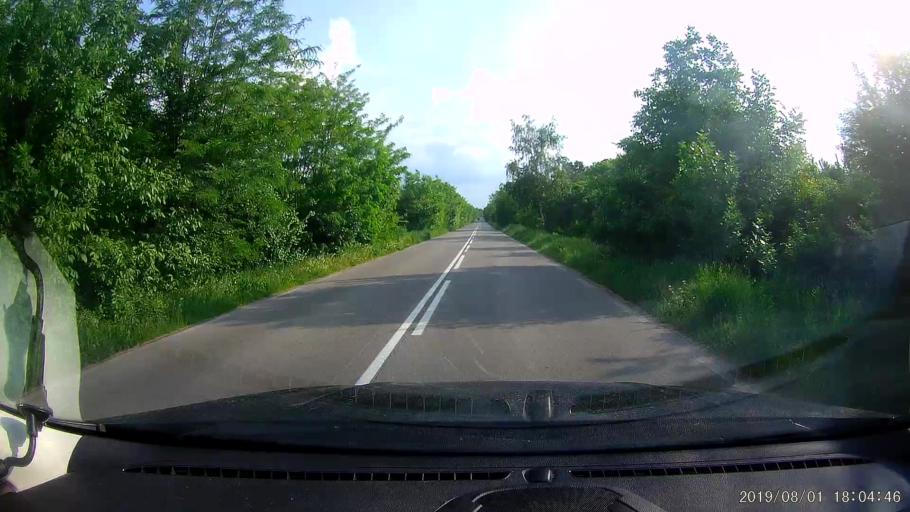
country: BG
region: Silistra
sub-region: Obshtina Alfatar
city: Alfatar
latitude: 43.9030
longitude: 27.2729
